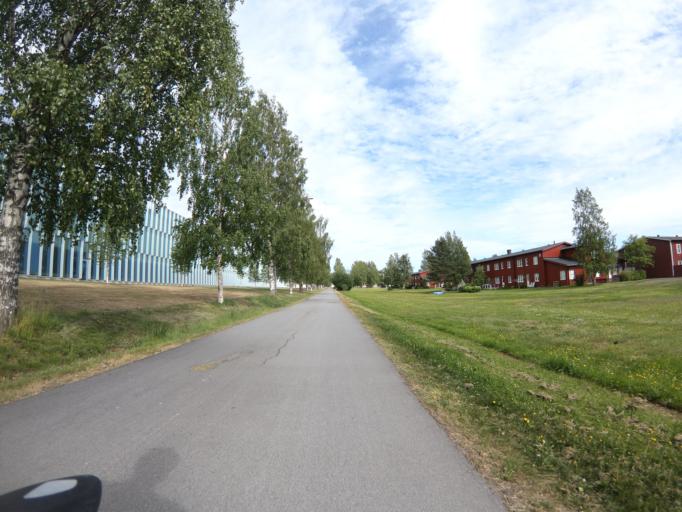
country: SE
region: Vaesterbotten
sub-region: Umea Kommun
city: Umea
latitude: 63.8189
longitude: 20.2549
